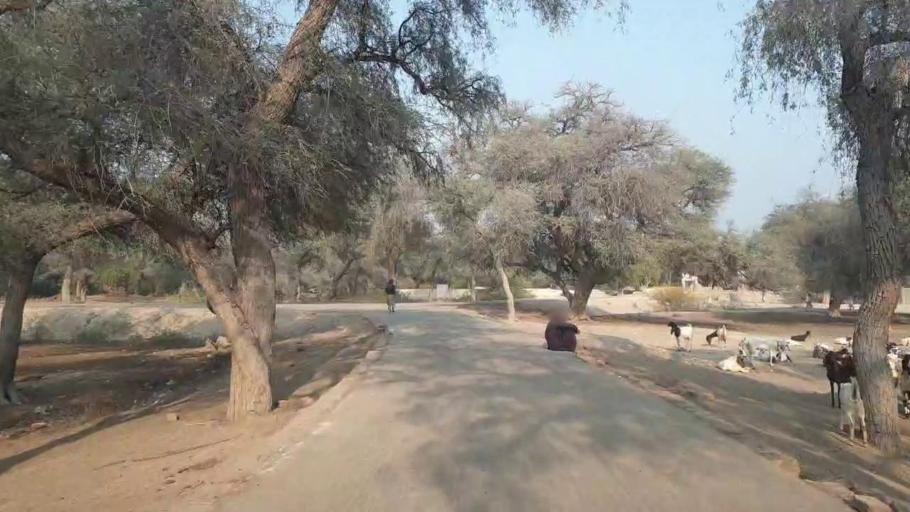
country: PK
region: Sindh
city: Hala
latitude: 25.7916
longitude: 68.3954
